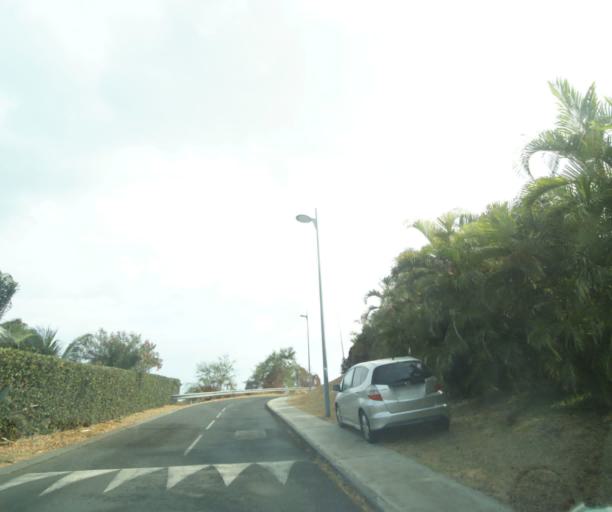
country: RE
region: Reunion
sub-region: Reunion
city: Saint-Paul
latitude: -21.0471
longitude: 55.2250
